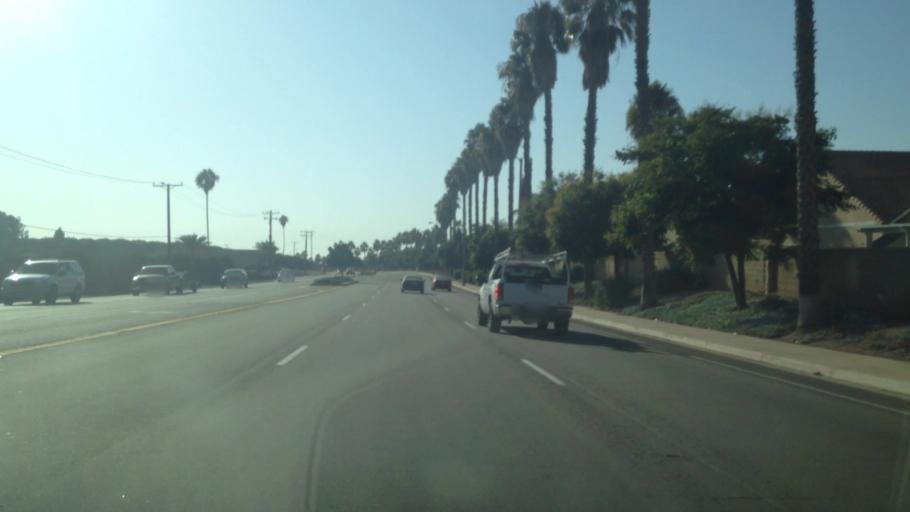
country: US
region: California
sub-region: Riverside County
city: Woodcrest
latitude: 33.8886
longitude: -117.3146
